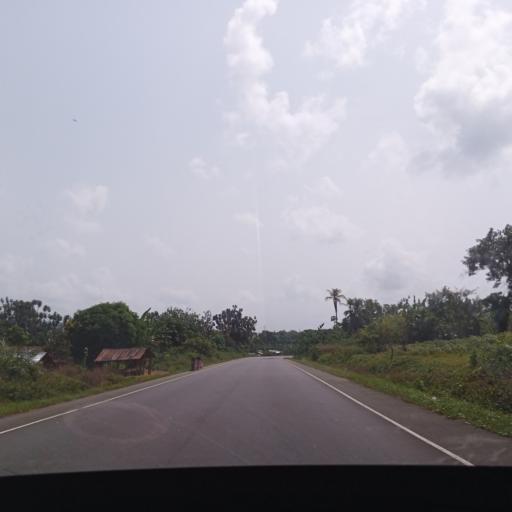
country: LR
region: Margibi
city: Kakata
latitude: 6.2322
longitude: -10.2802
